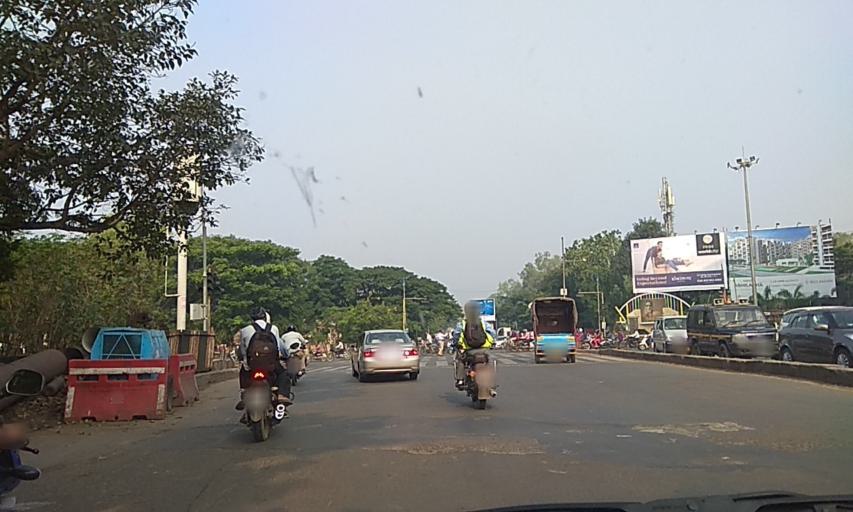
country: IN
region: Maharashtra
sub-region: Pune Division
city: Shivaji Nagar
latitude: 18.5446
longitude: 73.8775
